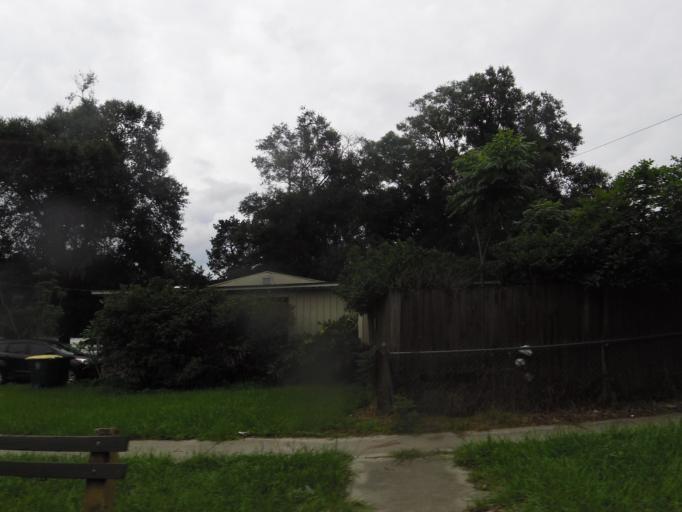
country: US
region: Florida
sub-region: Duval County
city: Jacksonville
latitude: 30.2823
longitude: -81.5441
